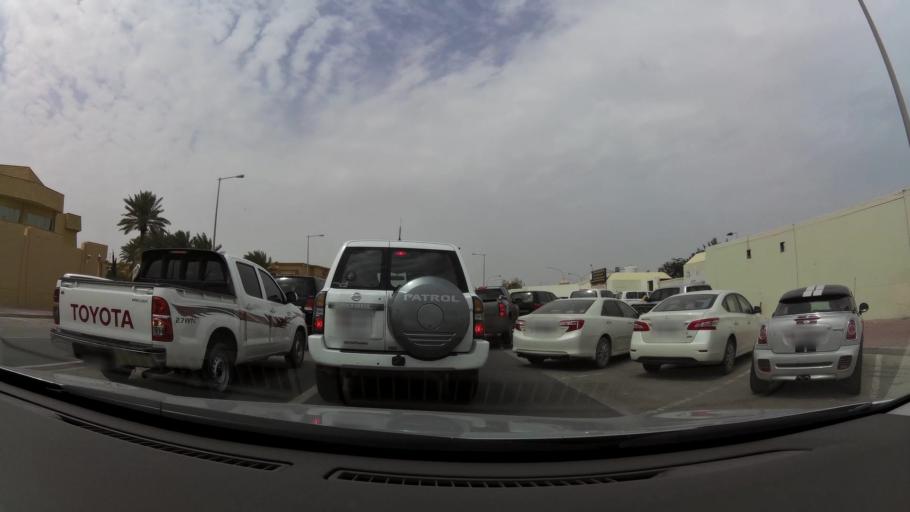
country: QA
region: Baladiyat ar Rayyan
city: Ar Rayyan
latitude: 25.3301
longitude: 51.4769
